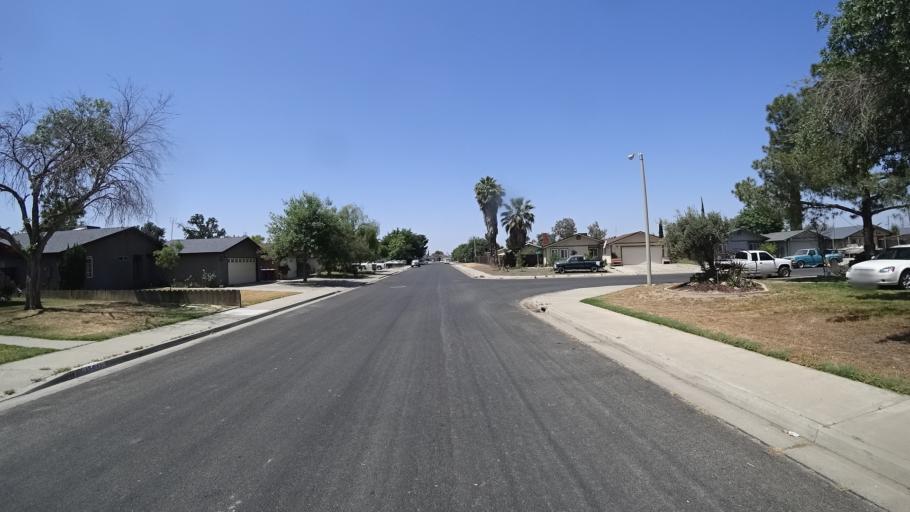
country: US
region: California
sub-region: Kings County
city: Armona
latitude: 36.3082
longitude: -119.7027
